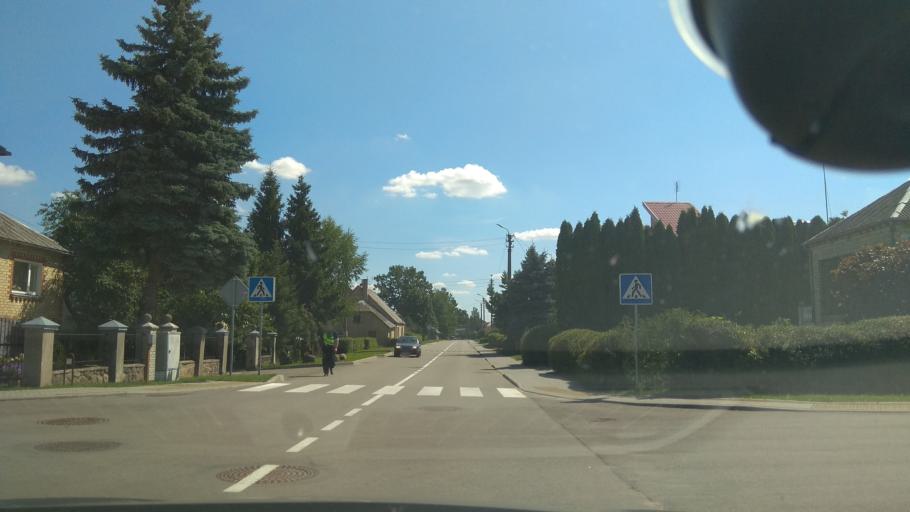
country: LT
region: Siauliu apskritis
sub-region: Joniskis
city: Joniskis
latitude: 56.2473
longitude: 23.6102
